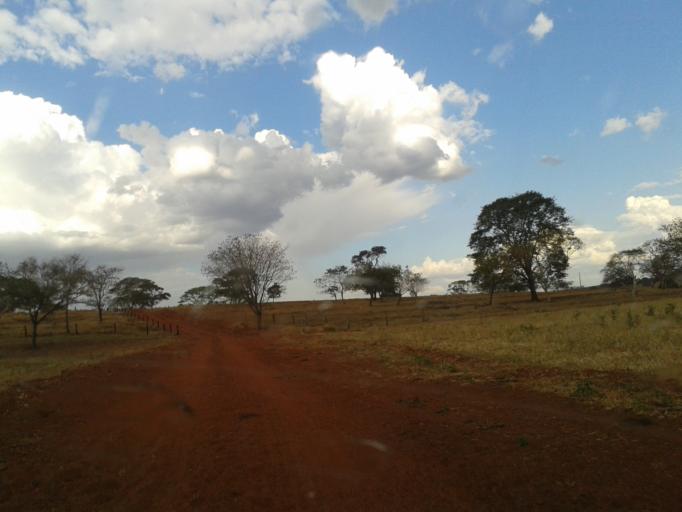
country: BR
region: Minas Gerais
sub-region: Santa Vitoria
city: Santa Vitoria
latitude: -19.1710
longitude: -49.9652
